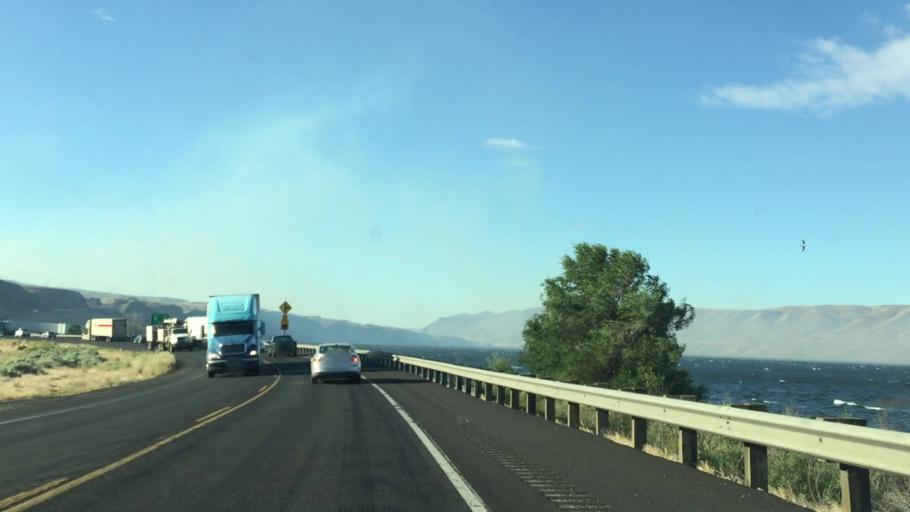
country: US
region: Washington
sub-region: Grant County
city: Mattawa
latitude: 46.9332
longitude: -119.9588
